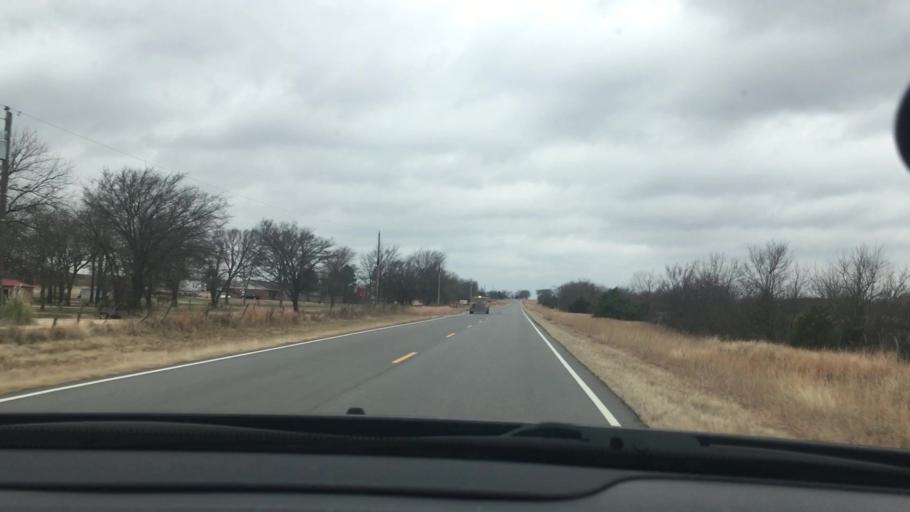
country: US
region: Oklahoma
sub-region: Atoka County
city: Atoka
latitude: 34.3747
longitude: -96.1855
